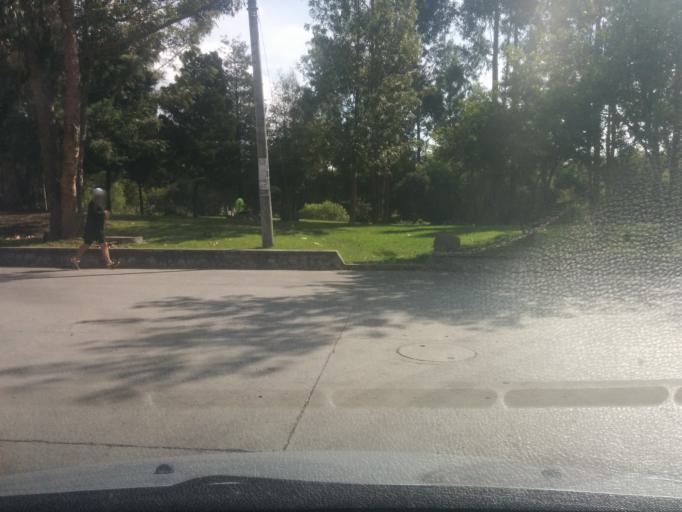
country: EC
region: Azuay
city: Cuenca
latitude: -2.8861
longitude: -78.9571
